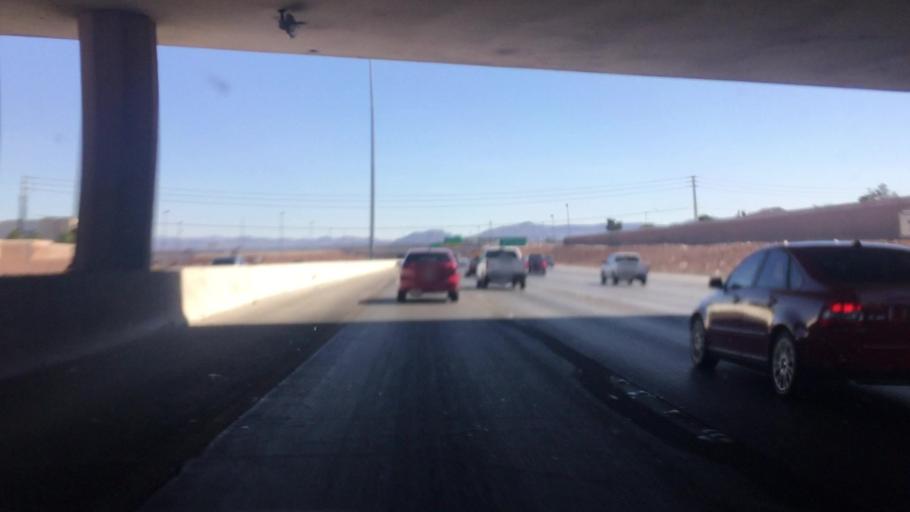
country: US
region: Nevada
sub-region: Clark County
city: Paradise
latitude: 36.0664
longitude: -115.1902
